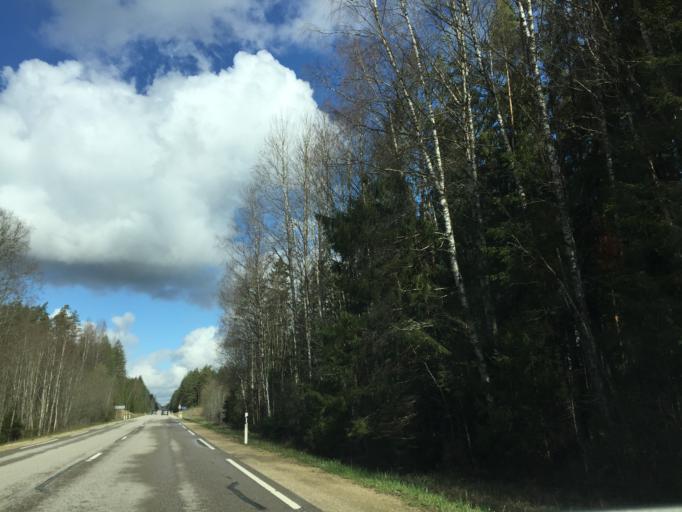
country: LV
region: Apes Novads
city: Ape
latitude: 57.5007
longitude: 26.7884
